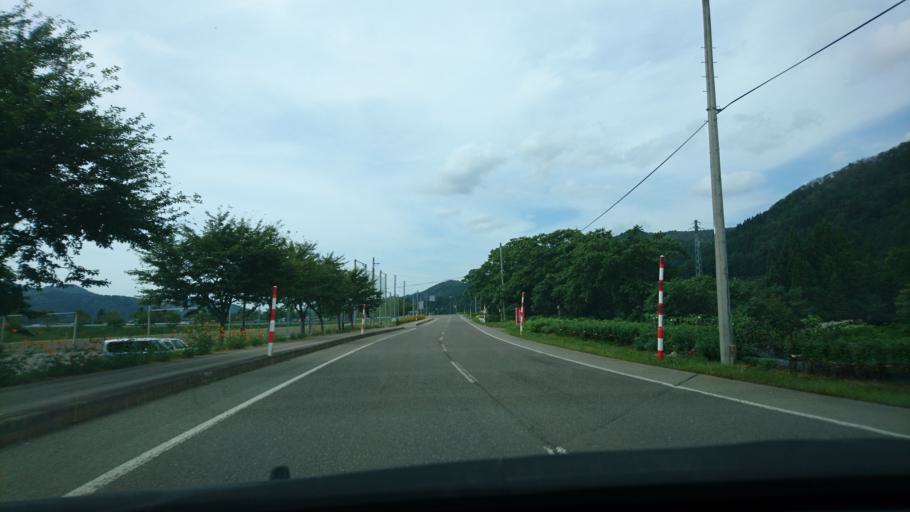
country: JP
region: Akita
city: Yuzawa
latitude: 39.1807
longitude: 140.6516
